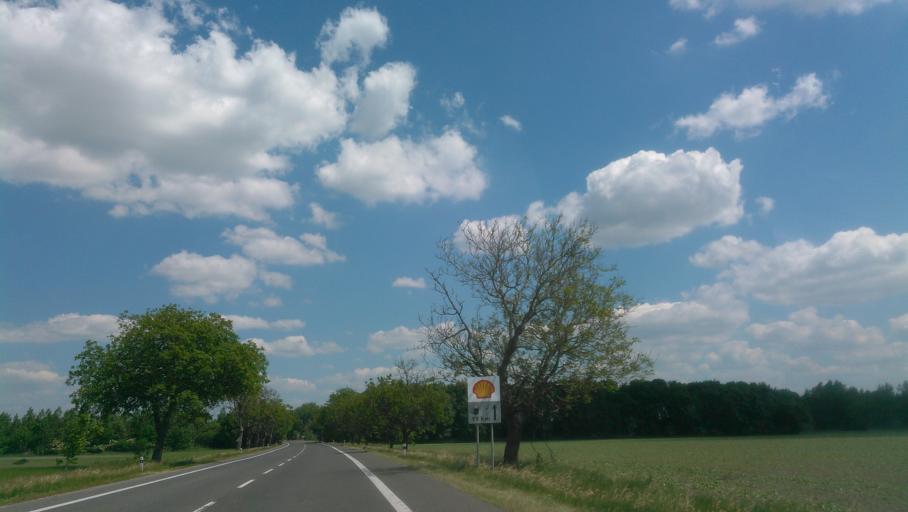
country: SK
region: Trnavsky
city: Samorin
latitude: 47.9994
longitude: 17.4268
